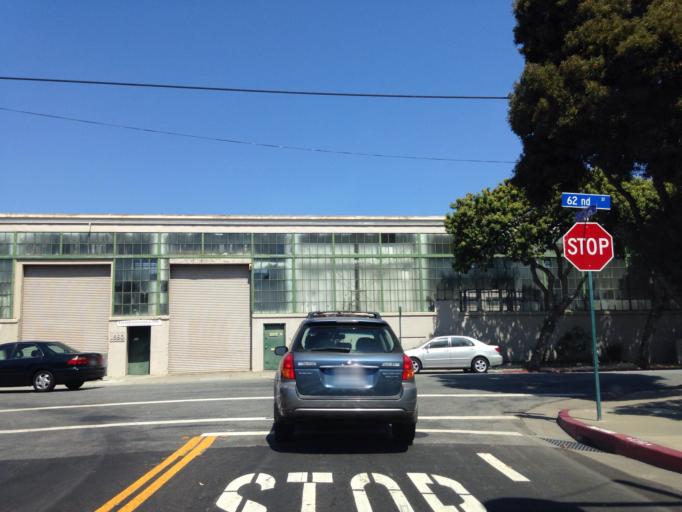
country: US
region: California
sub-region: Alameda County
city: Emeryville
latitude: 37.8424
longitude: -122.2918
